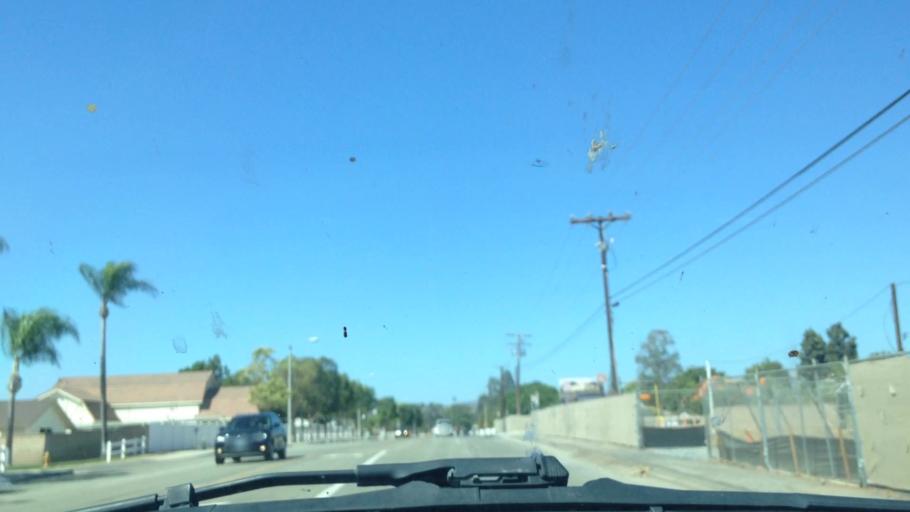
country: US
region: California
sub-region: Orange County
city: Yorba Linda
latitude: 33.8759
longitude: -117.8160
